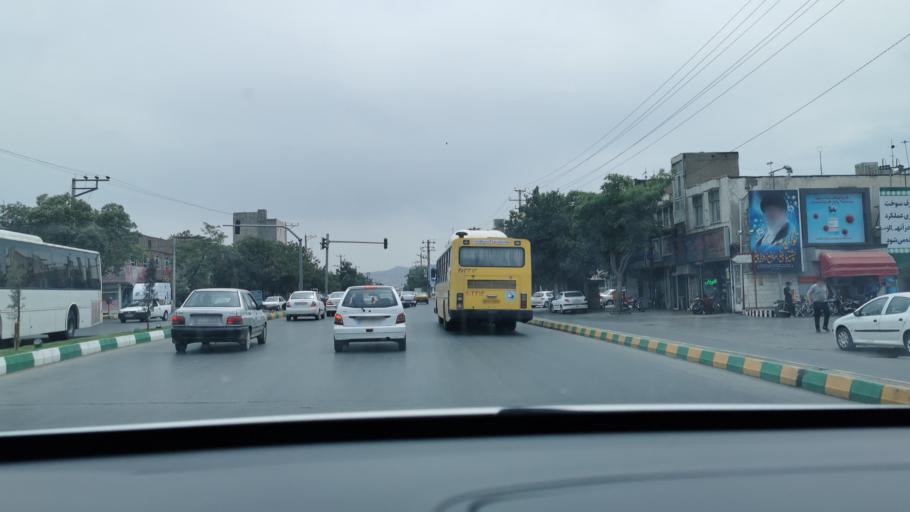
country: IR
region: Razavi Khorasan
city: Mashhad
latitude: 36.3230
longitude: 59.6214
